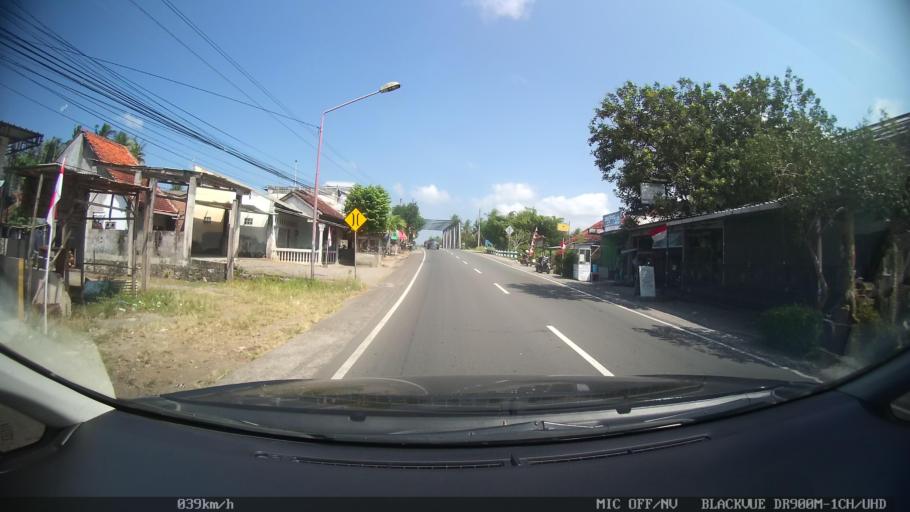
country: ID
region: Daerah Istimewa Yogyakarta
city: Srandakan
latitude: -7.8935
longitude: 110.1421
